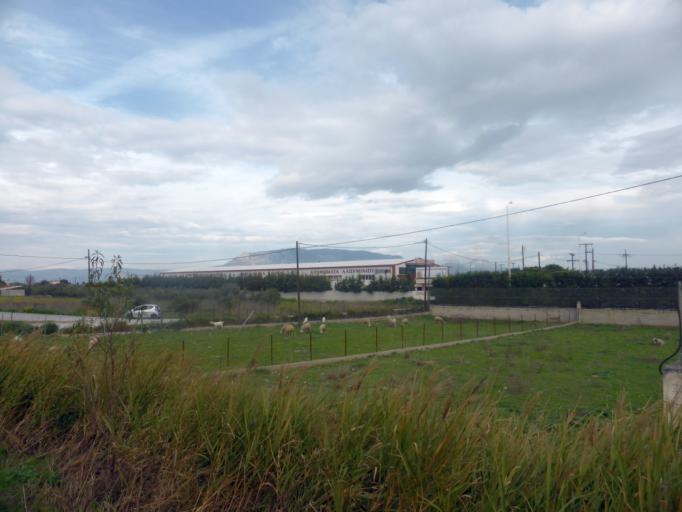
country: GR
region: Peloponnese
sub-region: Nomos Korinthias
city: Arkhaia Korinthos
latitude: 37.9175
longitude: 22.8845
